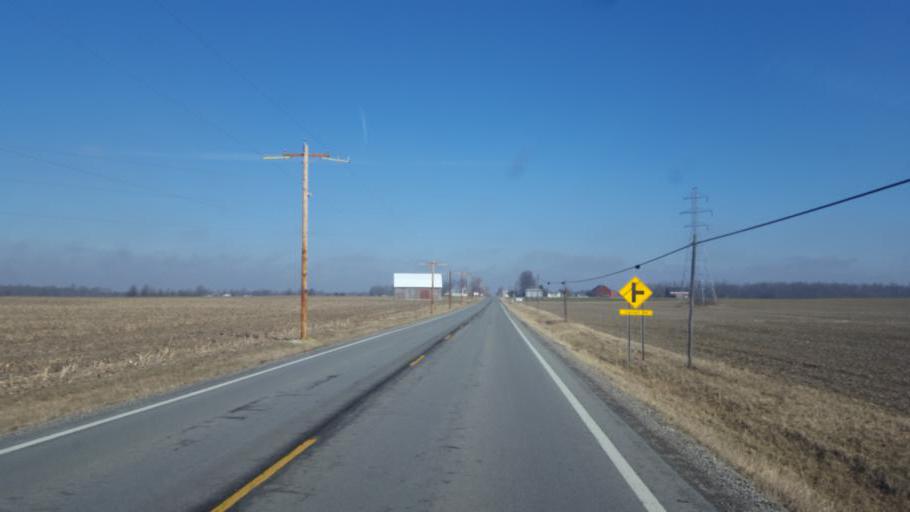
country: US
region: Ohio
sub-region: Crawford County
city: Bucyrus
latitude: 40.8463
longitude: -82.9686
